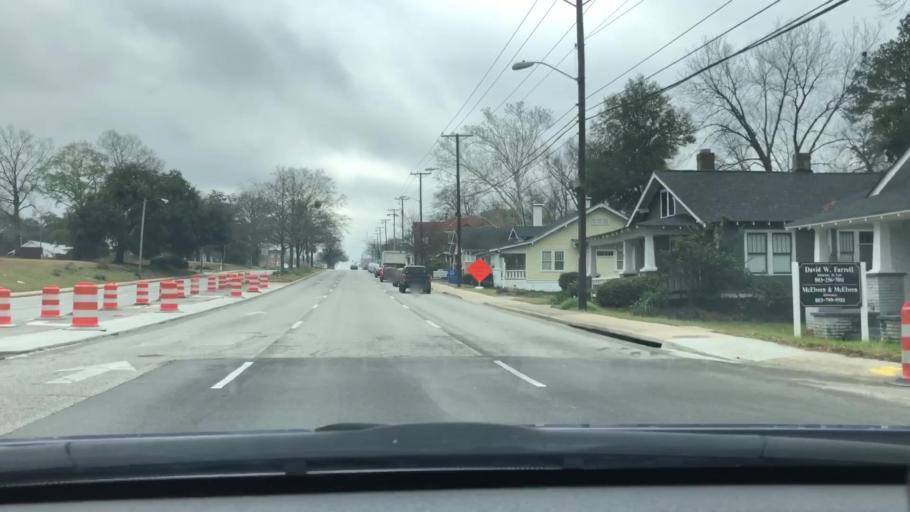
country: US
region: South Carolina
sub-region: Richland County
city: Columbia
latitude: 34.0182
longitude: -81.0357
